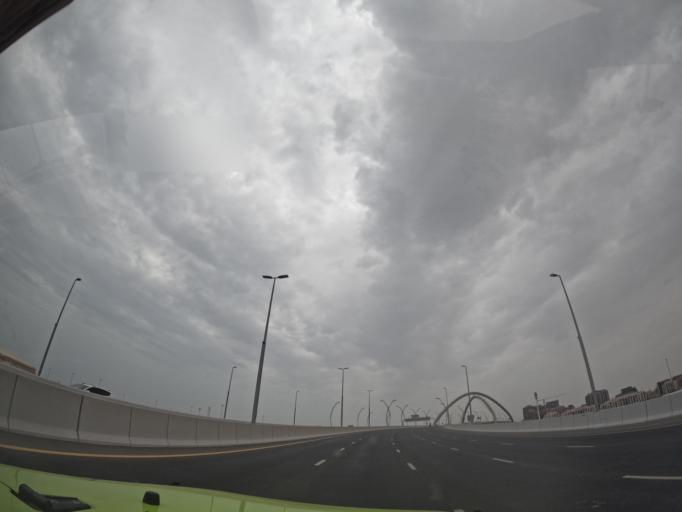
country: AE
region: Ash Shariqah
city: Sharjah
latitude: 25.2726
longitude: 55.2909
